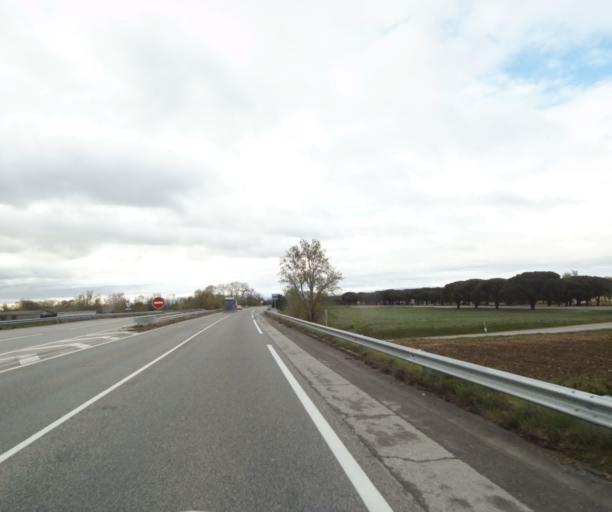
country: FR
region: Midi-Pyrenees
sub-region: Departement de l'Ariege
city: Saverdun
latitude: 43.2279
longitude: 1.6052
